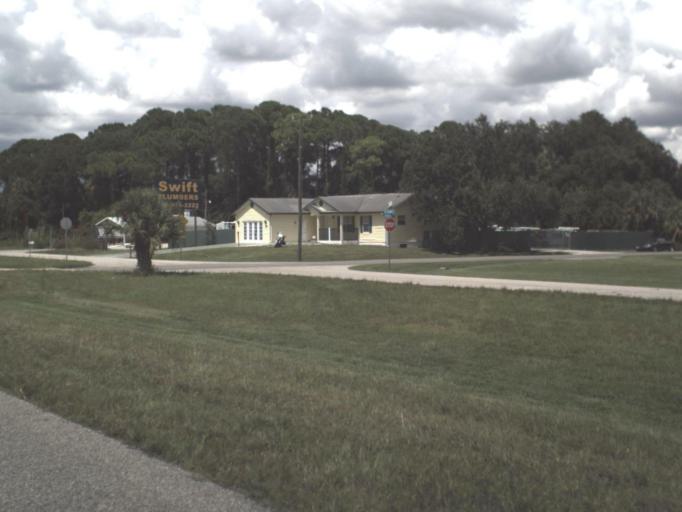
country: US
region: Florida
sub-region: Sarasota County
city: North Port
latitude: 27.0255
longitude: -82.1943
